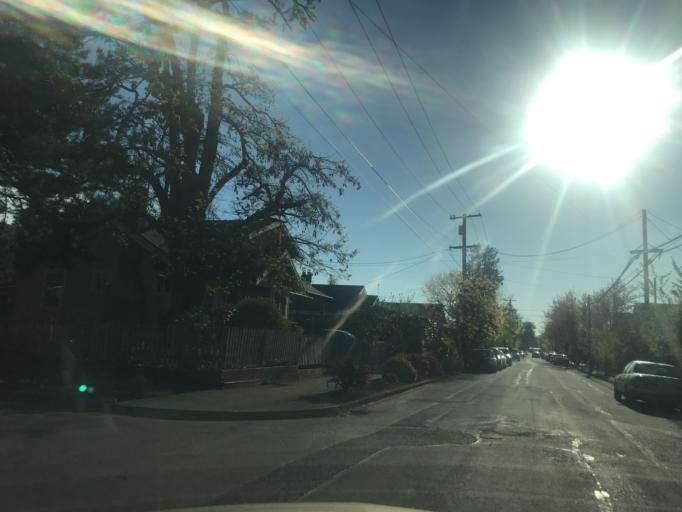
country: US
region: Oregon
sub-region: Multnomah County
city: Lents
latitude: 45.4866
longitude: -122.5853
